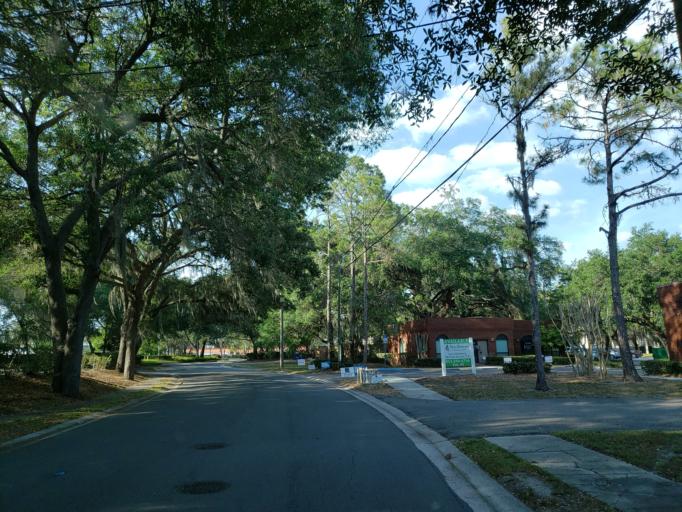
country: US
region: Florida
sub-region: Hillsborough County
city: Brandon
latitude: 27.9322
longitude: -82.2918
